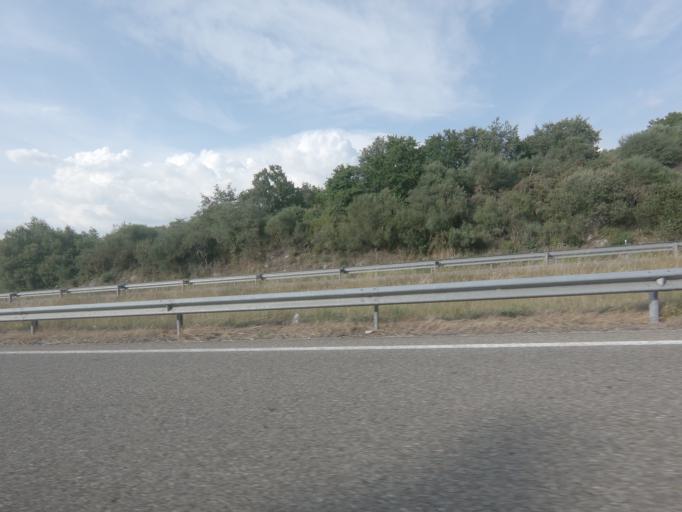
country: ES
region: Galicia
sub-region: Provincia de Ourense
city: Xinzo de Limia
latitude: 42.0683
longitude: -7.7039
